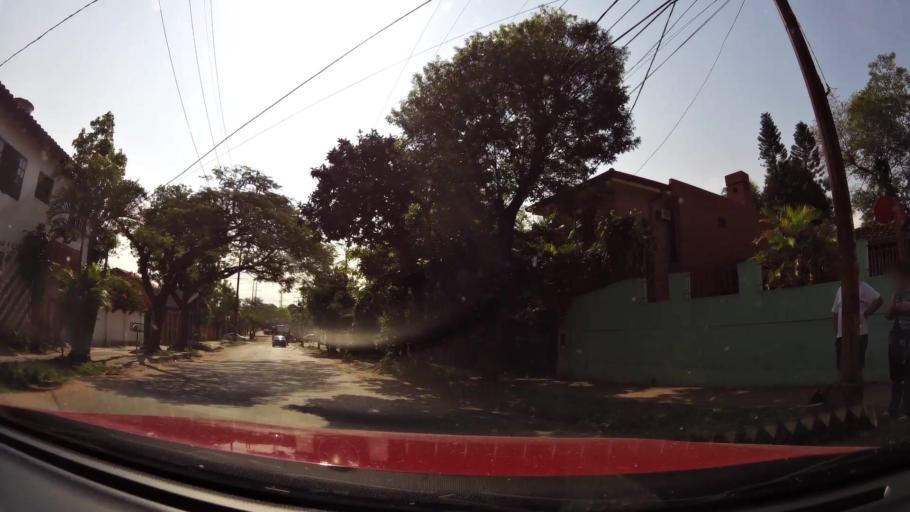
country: PY
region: Asuncion
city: Asuncion
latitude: -25.3232
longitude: -57.6344
